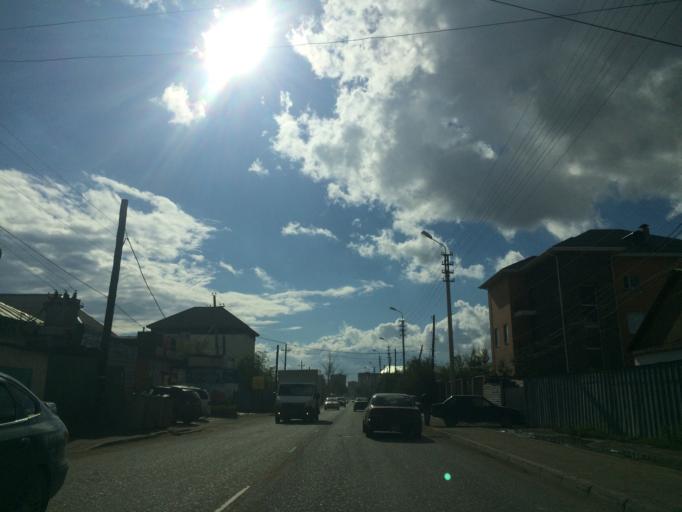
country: KZ
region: Astana Qalasy
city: Astana
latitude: 51.1897
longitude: 71.3856
